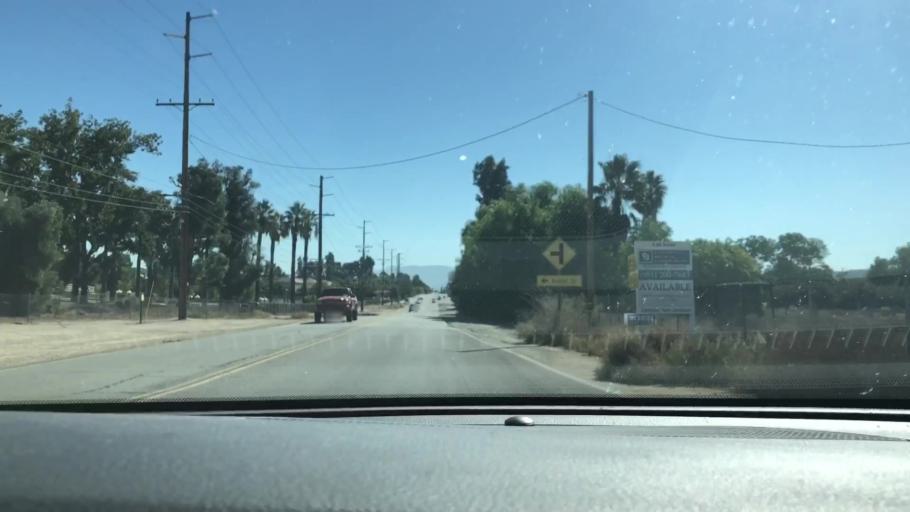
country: US
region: California
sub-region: Riverside County
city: Wildomar
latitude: 33.5988
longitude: -117.2656
